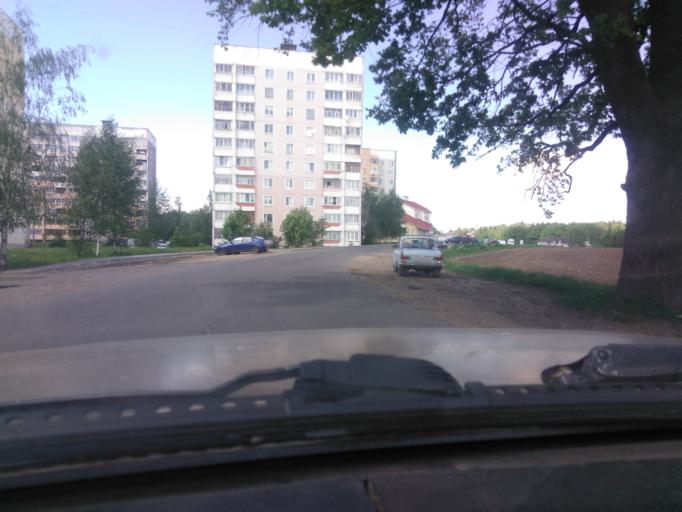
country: BY
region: Mogilev
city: Palykavichy Pyershyya
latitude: 53.9503
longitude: 30.3730
